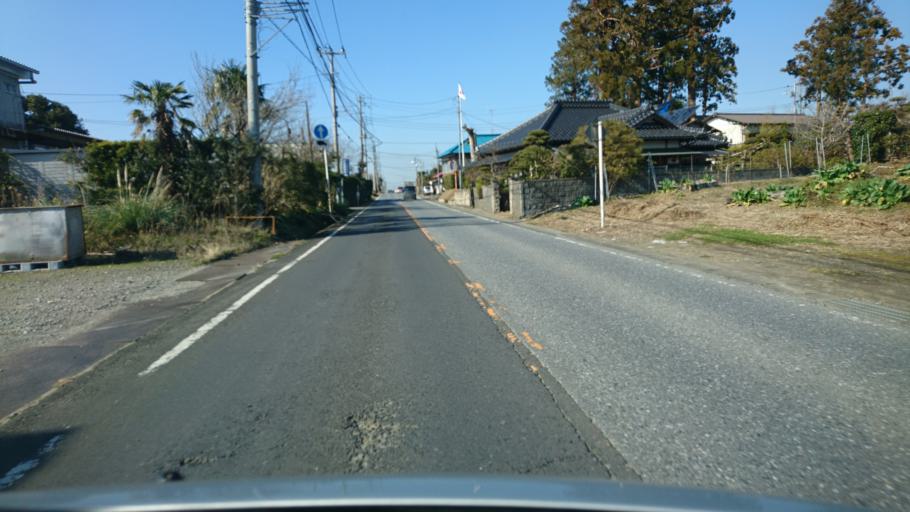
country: JP
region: Chiba
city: Kimitsu
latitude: 35.3017
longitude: 139.9737
